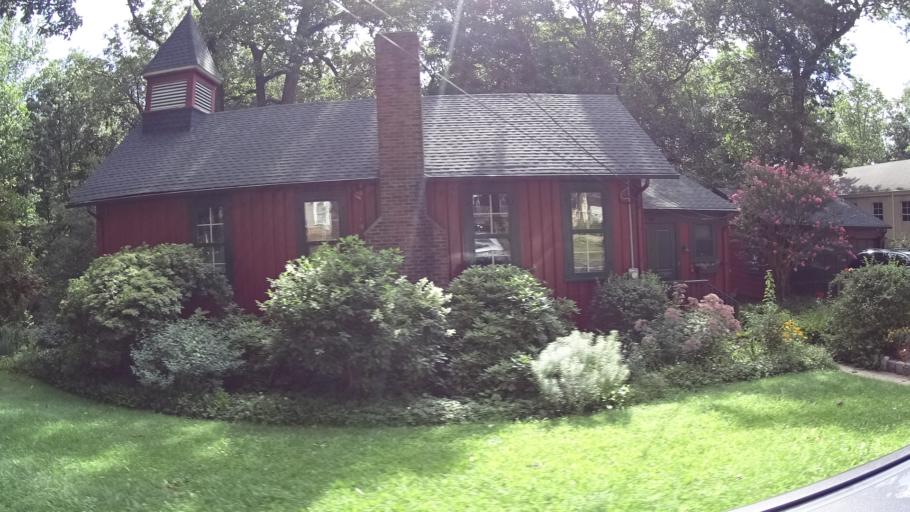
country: US
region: New Jersey
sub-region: Union County
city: New Providence
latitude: 40.6770
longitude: -74.4092
